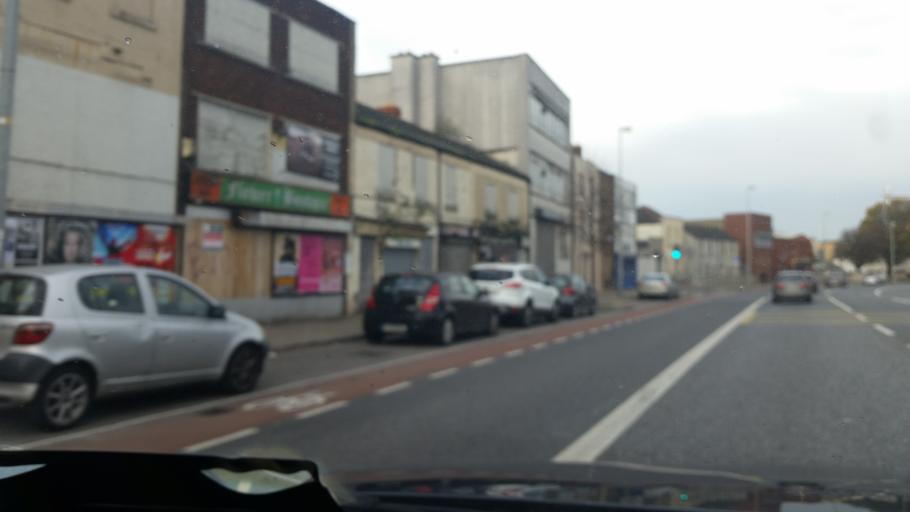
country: IE
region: Leinster
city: Rialto
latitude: 53.3349
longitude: -6.2898
